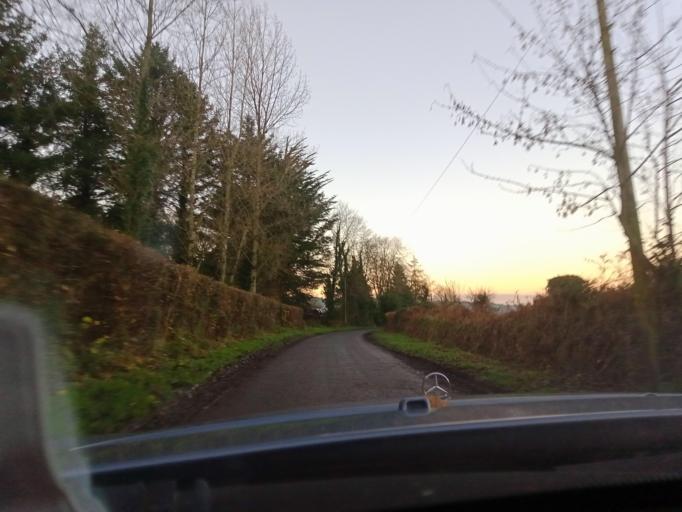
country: IE
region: Leinster
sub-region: Kilkenny
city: Thomastown
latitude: 52.4302
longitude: -7.1006
